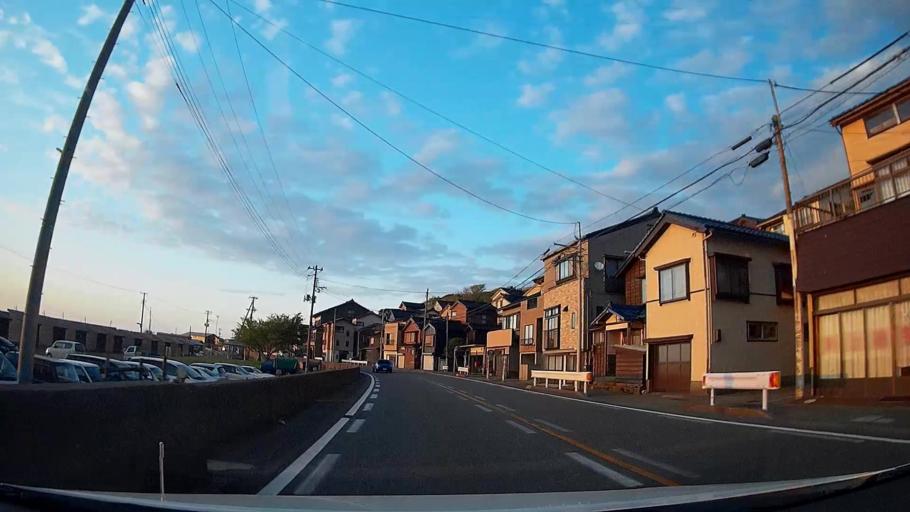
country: JP
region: Niigata
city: Itoigawa
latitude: 37.1098
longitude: 138.0006
